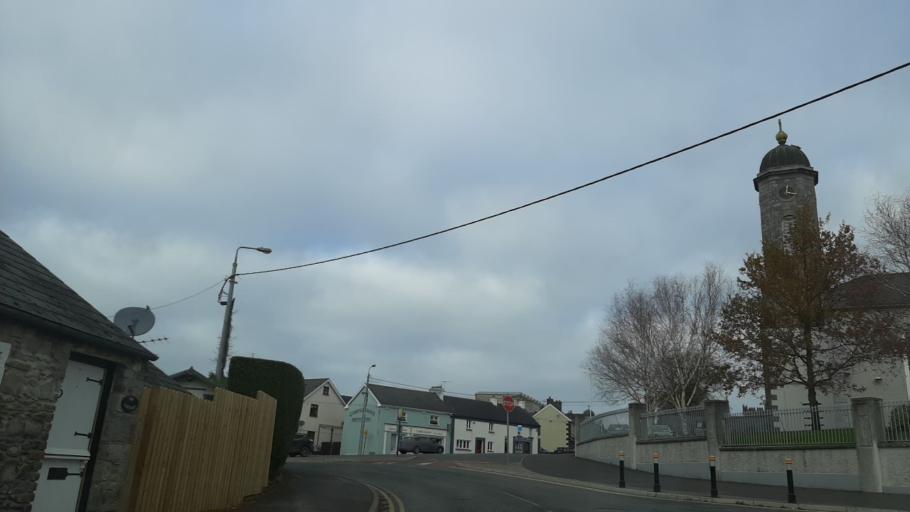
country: IE
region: Leinster
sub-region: Kildare
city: Kildare
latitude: 53.1549
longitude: -6.9110
